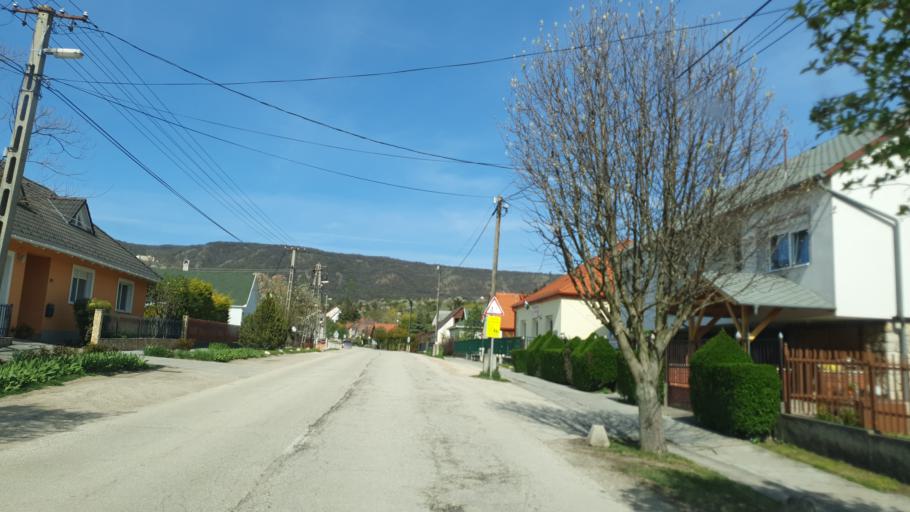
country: HU
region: Fejer
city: Bodajk
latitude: 47.3485
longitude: 18.2668
